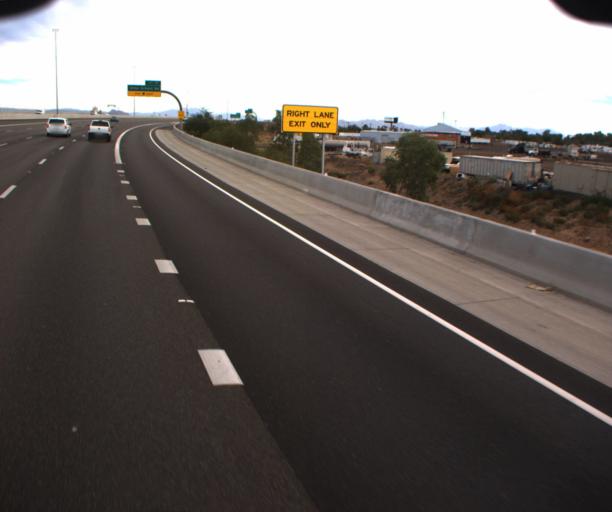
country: US
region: Arizona
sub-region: Maricopa County
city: Mesa
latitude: 33.4432
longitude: -111.8629
